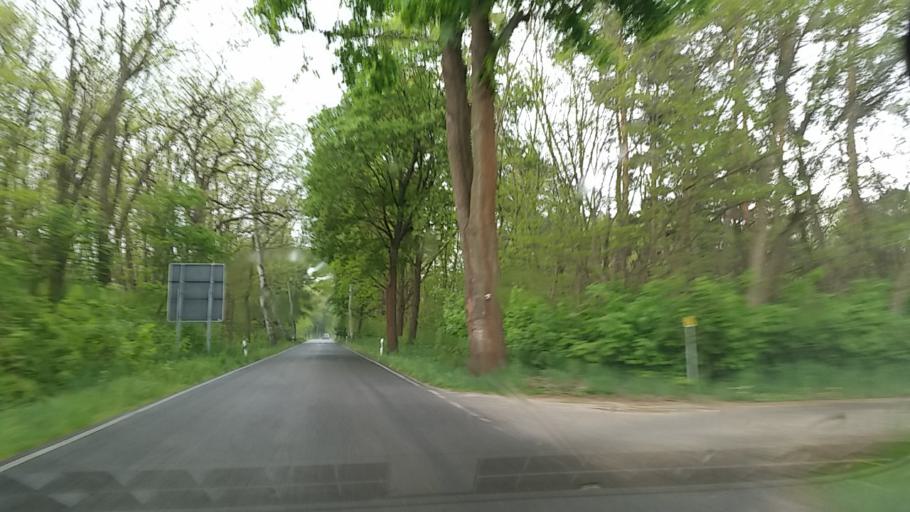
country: DE
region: Brandenburg
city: Diensdorf-Radlow
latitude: 52.2542
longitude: 14.0388
